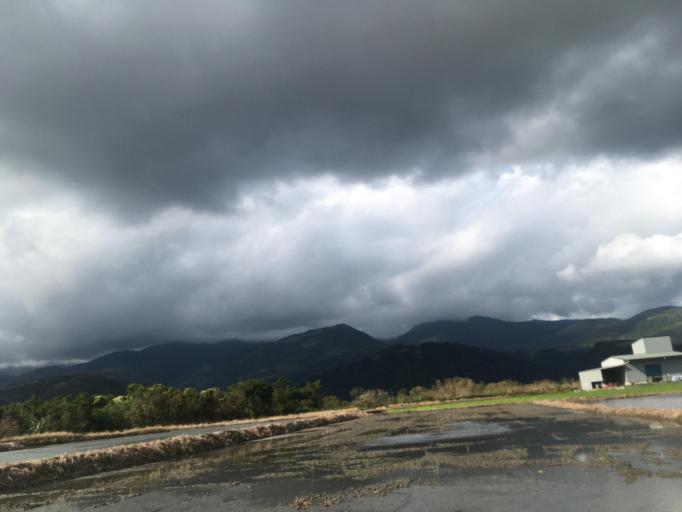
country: TW
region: Taiwan
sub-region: Yilan
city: Yilan
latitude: 24.6654
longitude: 121.6219
